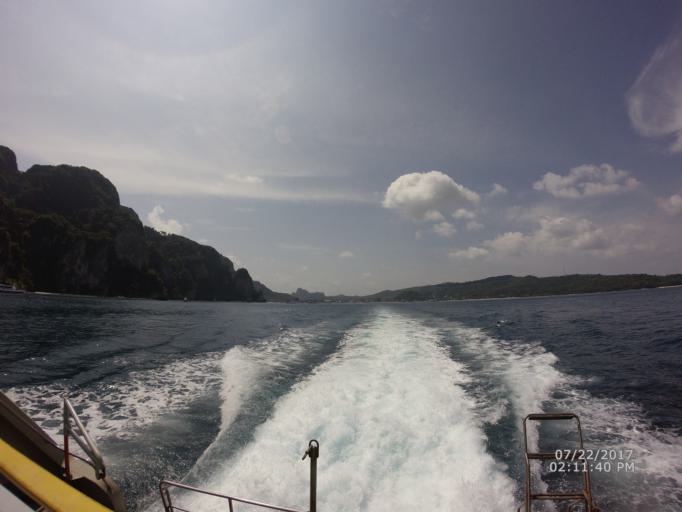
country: TH
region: Krabi
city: Saladan
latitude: 7.7208
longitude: 98.7724
